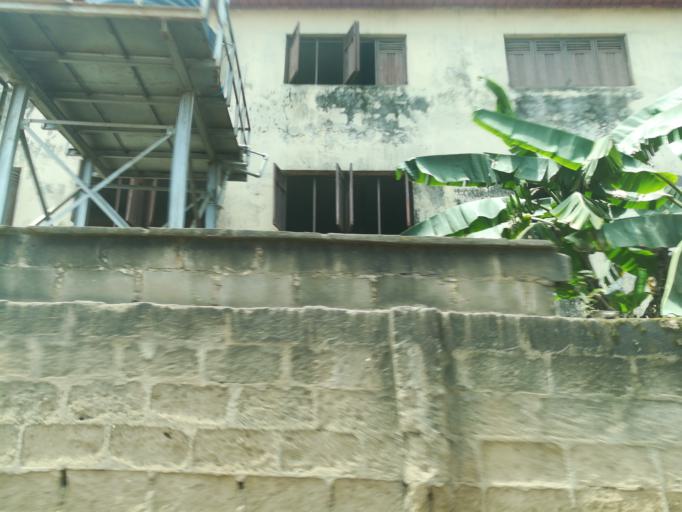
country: NG
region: Lagos
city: Ikorodu
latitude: 6.6183
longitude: 3.5008
